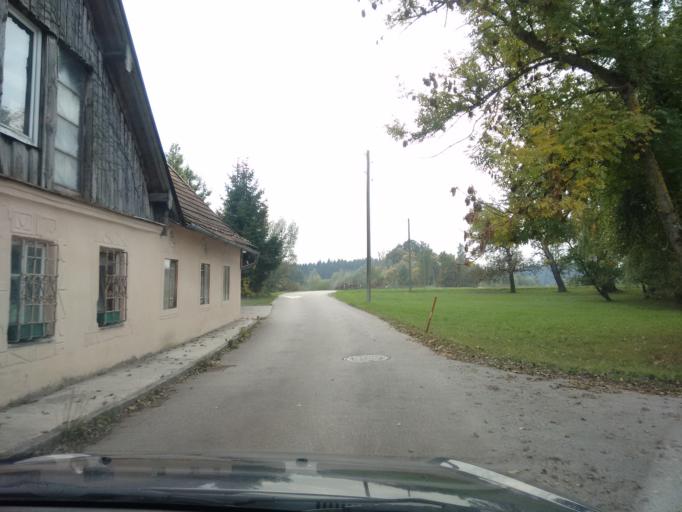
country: AT
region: Upper Austria
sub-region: Wels-Land
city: Offenhausen
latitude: 48.1661
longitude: 13.8638
